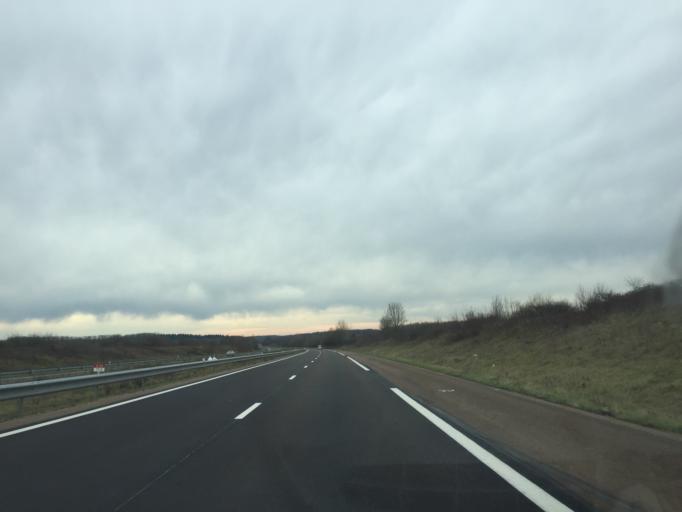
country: FR
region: Franche-Comte
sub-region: Departement du Jura
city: Bletterans
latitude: 46.8344
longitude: 5.5509
